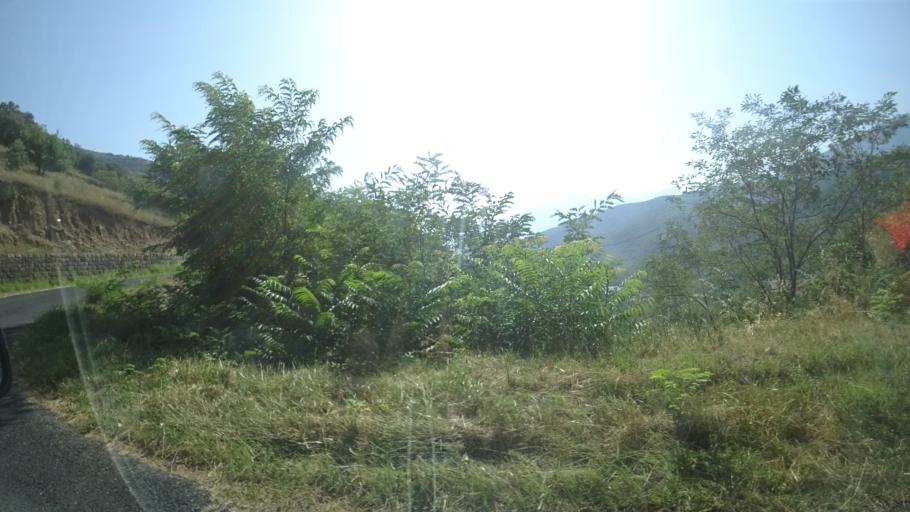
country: FR
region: Languedoc-Roussillon
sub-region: Departement des Pyrenees-Orientales
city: Vernet-les-Bains
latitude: 42.5628
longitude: 2.2853
